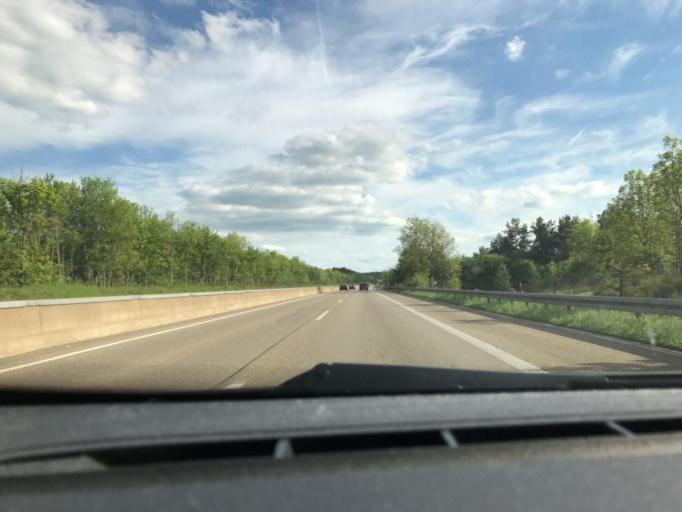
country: DE
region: North Rhine-Westphalia
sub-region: Regierungsbezirk Koln
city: Mechernich
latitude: 50.5483
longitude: 6.6785
